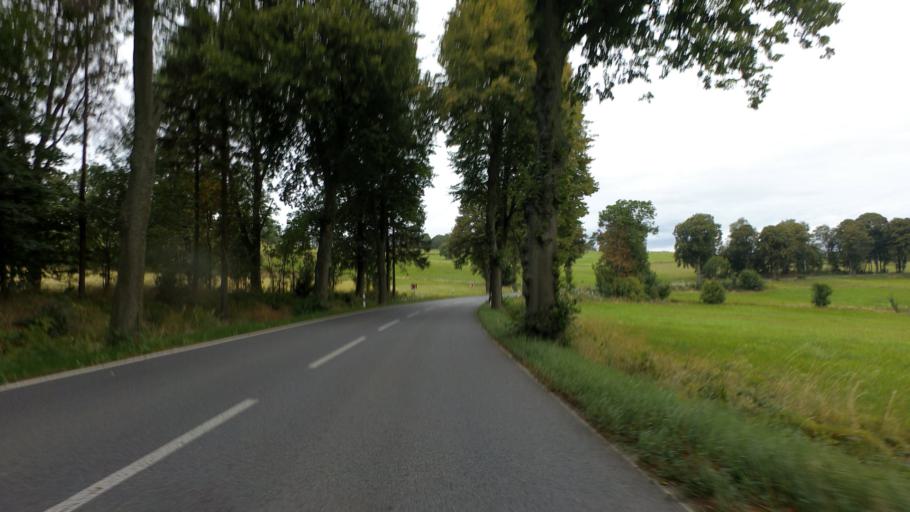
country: DE
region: Saxony
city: Berthelsdorf
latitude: 51.0797
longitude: 14.2013
